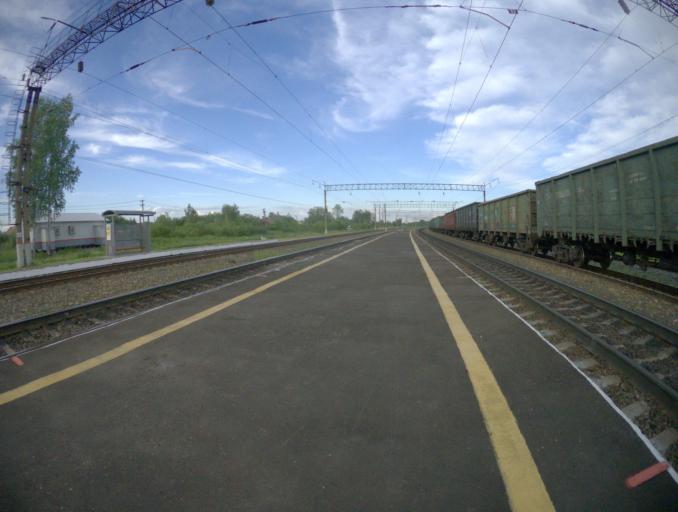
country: RU
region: Vladimir
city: Zolotkovo
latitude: 55.5041
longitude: 40.9605
